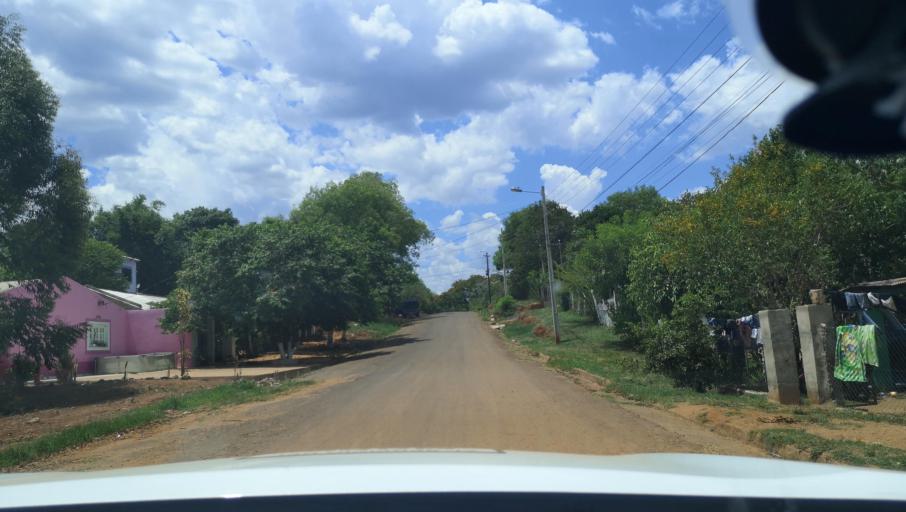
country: PY
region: Itapua
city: Carmen del Parana
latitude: -27.1695
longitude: -56.2486
